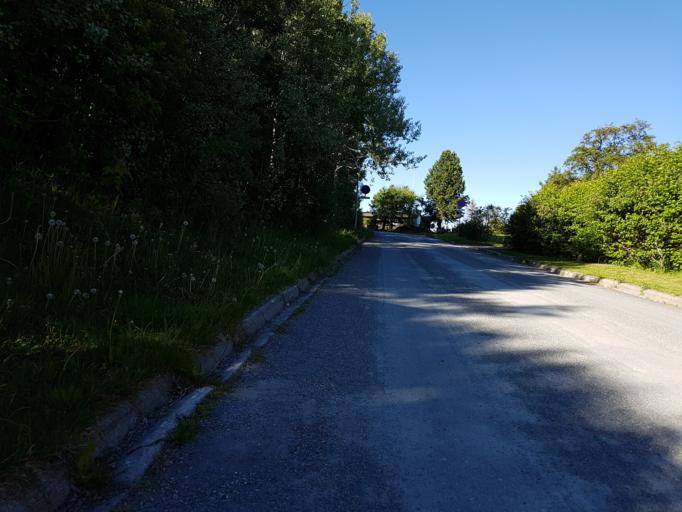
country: NO
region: Sor-Trondelag
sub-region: Trondheim
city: Trondheim
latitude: 63.4193
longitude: 10.3648
